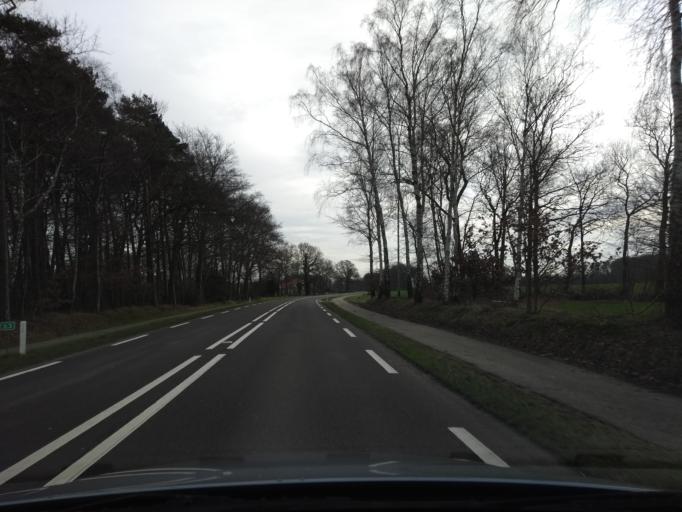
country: NL
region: Overijssel
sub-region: Gemeente Hof van Twente
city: Delden
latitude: 52.2756
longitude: 6.6840
